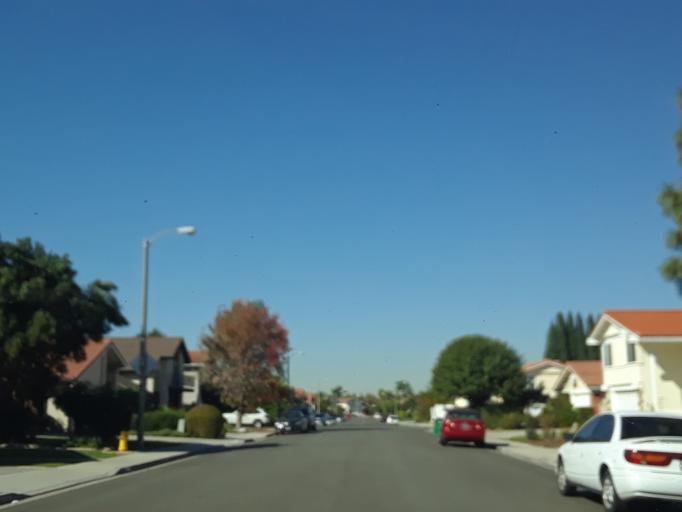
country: US
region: California
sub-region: Orange County
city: Irvine
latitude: 33.7007
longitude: -117.7943
